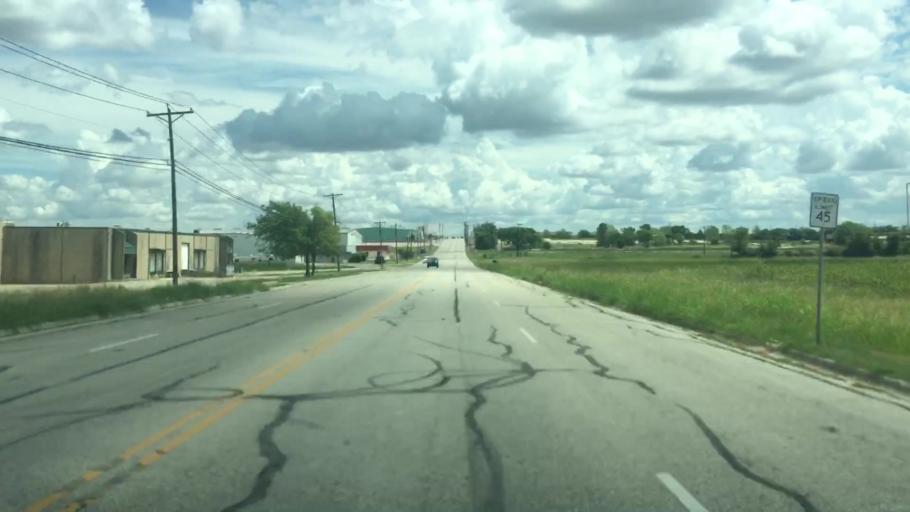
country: US
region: Texas
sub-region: Bell County
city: Temple
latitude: 31.1296
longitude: -97.3529
